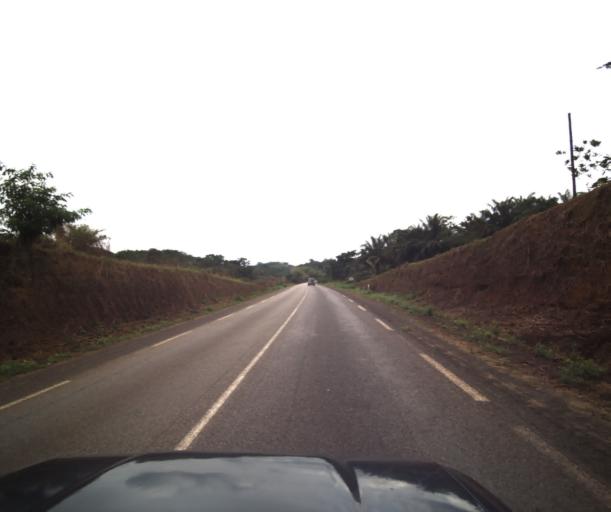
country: CM
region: Littoral
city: Edea
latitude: 3.8365
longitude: 10.4457
